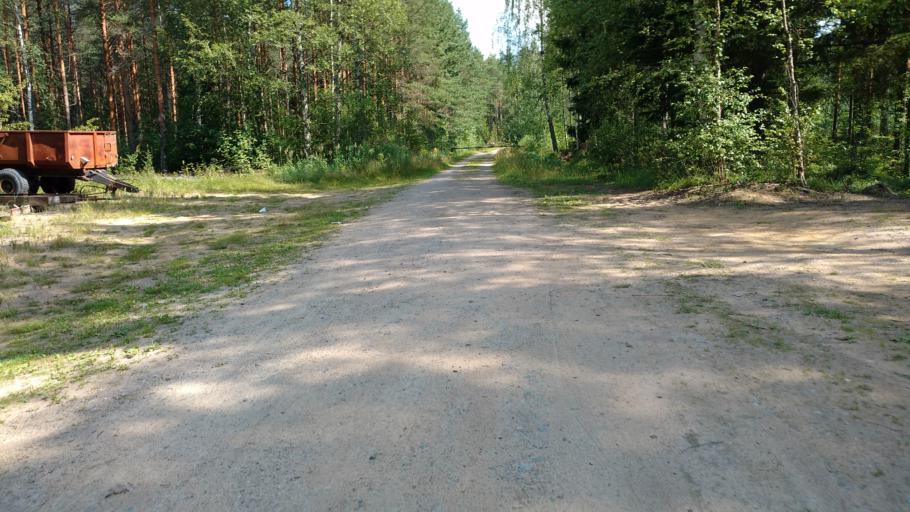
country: FI
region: Varsinais-Suomi
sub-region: Salo
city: Pertteli
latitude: 60.4065
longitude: 23.2030
